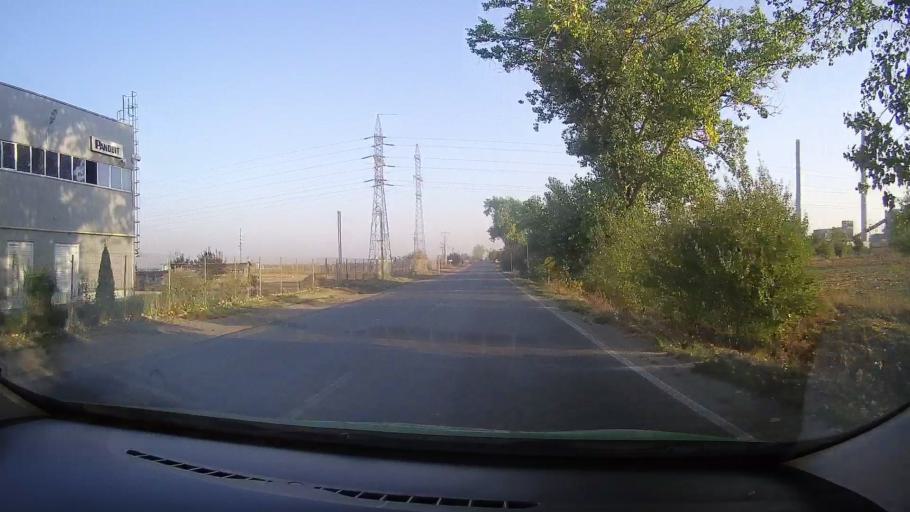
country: RO
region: Arad
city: Arad
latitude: 46.2178
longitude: 21.3205
